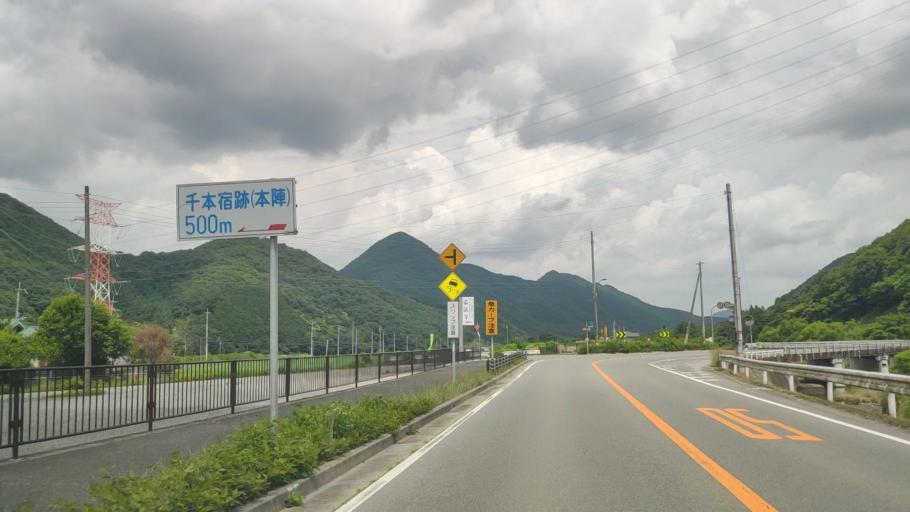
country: JP
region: Hyogo
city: Yamazakicho-nakabirose
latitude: 34.9411
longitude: 134.4950
